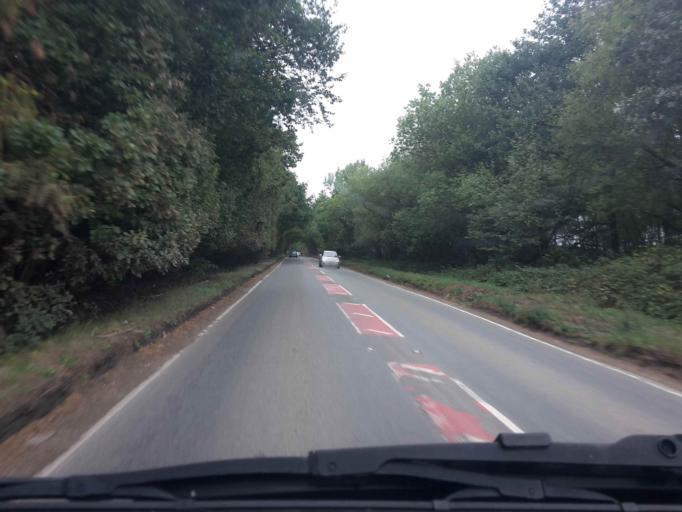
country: GB
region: England
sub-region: Hampshire
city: Eversley
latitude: 51.3264
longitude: -0.8717
